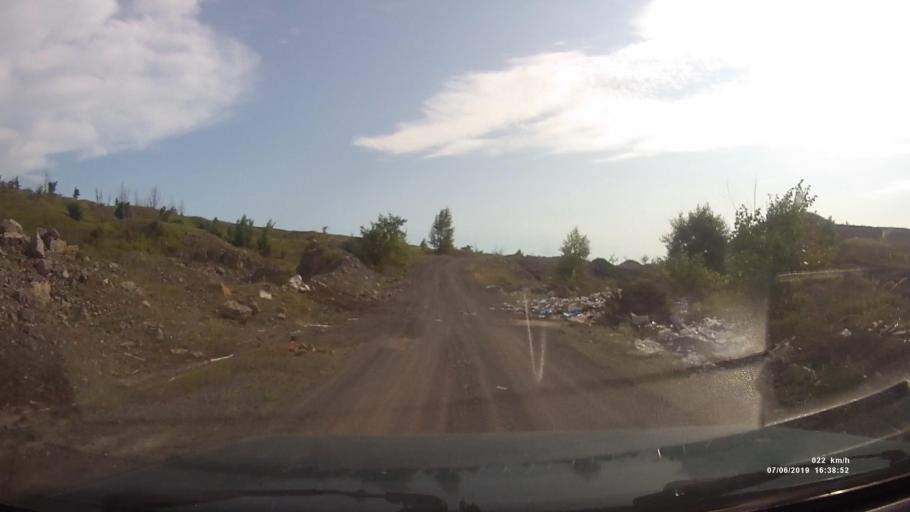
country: RU
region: Rostov
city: Staraya Stanitsa
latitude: 48.2491
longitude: 40.3463
